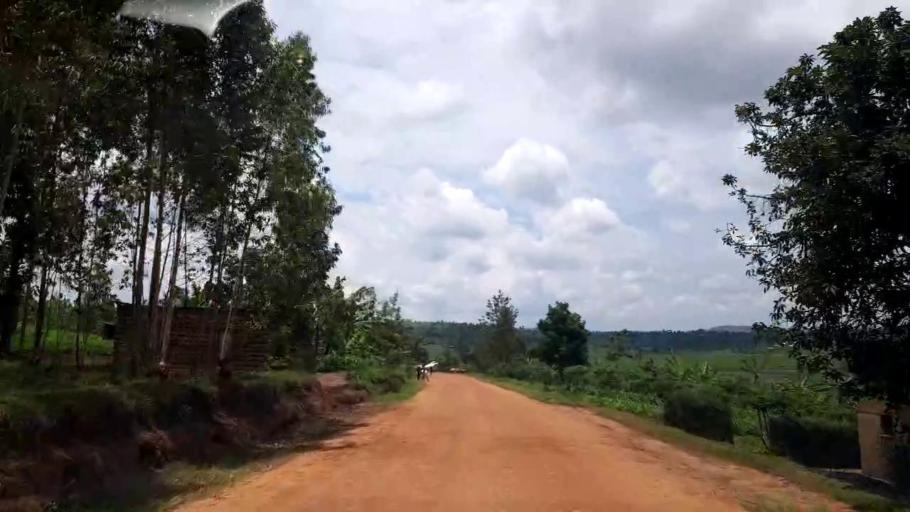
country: RW
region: Northern Province
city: Byumba
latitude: -1.5698
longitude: 30.3009
